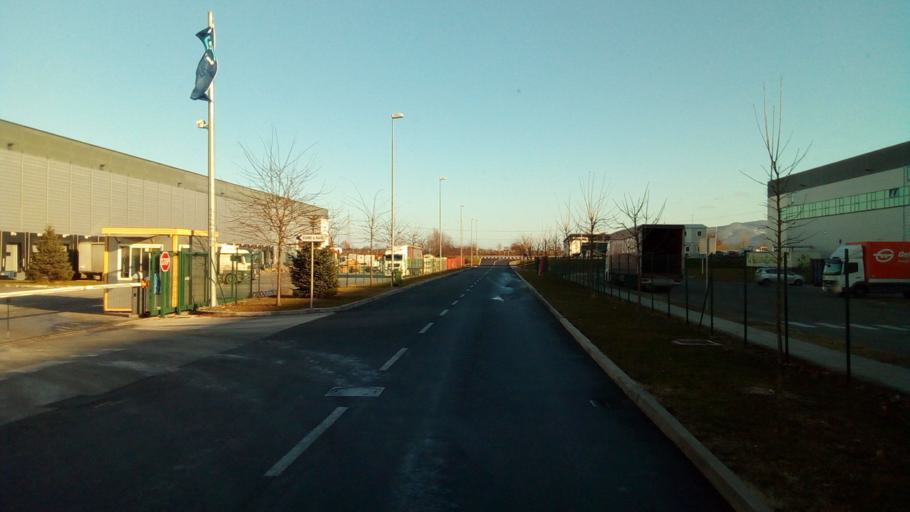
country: HR
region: Zagrebacka
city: Bestovje
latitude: 45.8030
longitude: 15.7733
